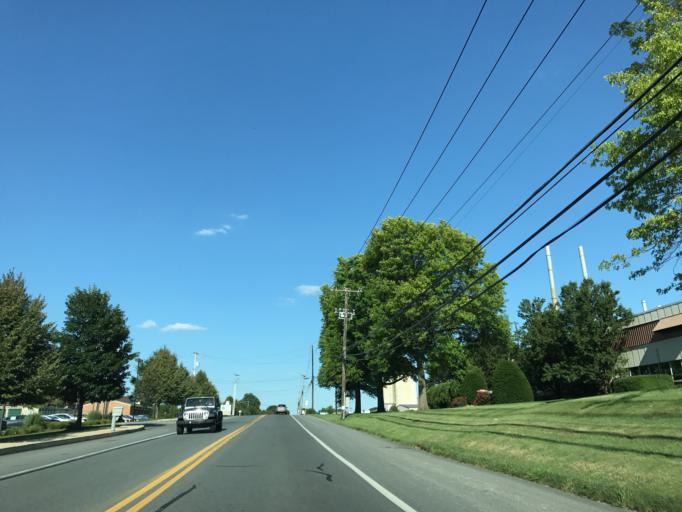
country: US
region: Pennsylvania
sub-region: Lancaster County
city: Mount Joy
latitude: 40.1100
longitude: -76.4774
